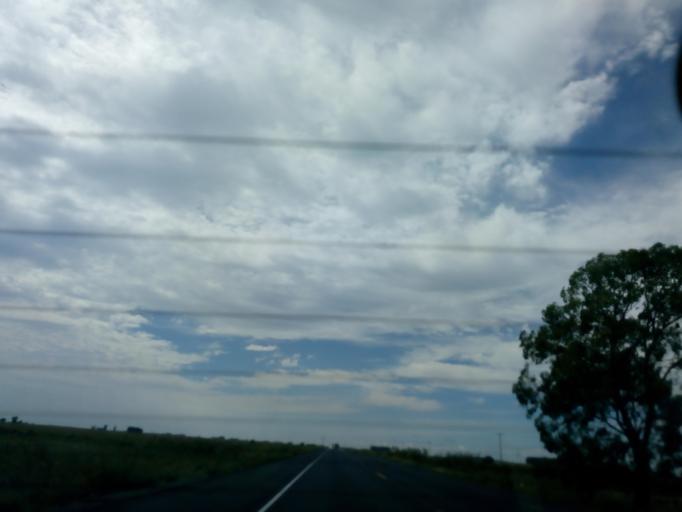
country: BR
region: Rio Grande do Sul
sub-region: Quarai
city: Quarai
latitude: -29.9796
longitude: -56.5448
